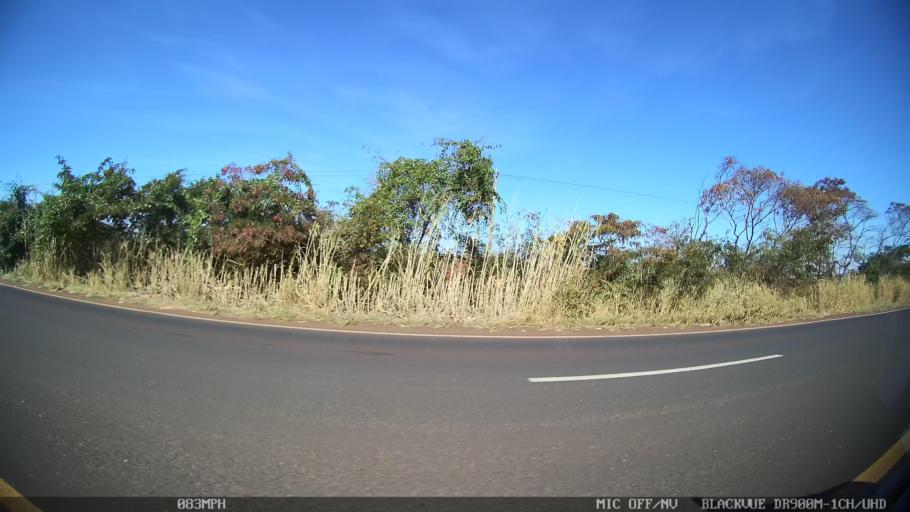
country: BR
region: Sao Paulo
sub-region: Barretos
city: Barretos
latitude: -20.5553
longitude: -48.6420
